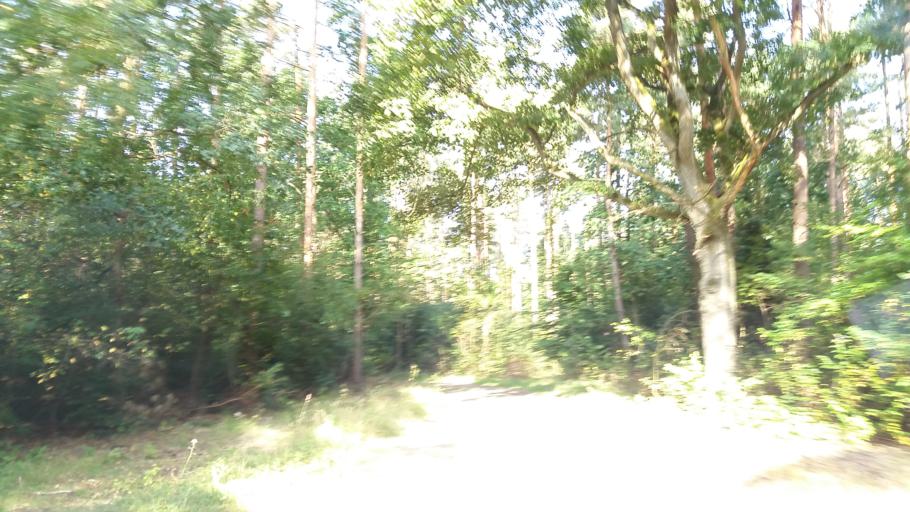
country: PL
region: West Pomeranian Voivodeship
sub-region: Powiat choszczenski
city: Choszczno
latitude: 53.2429
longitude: 15.4130
